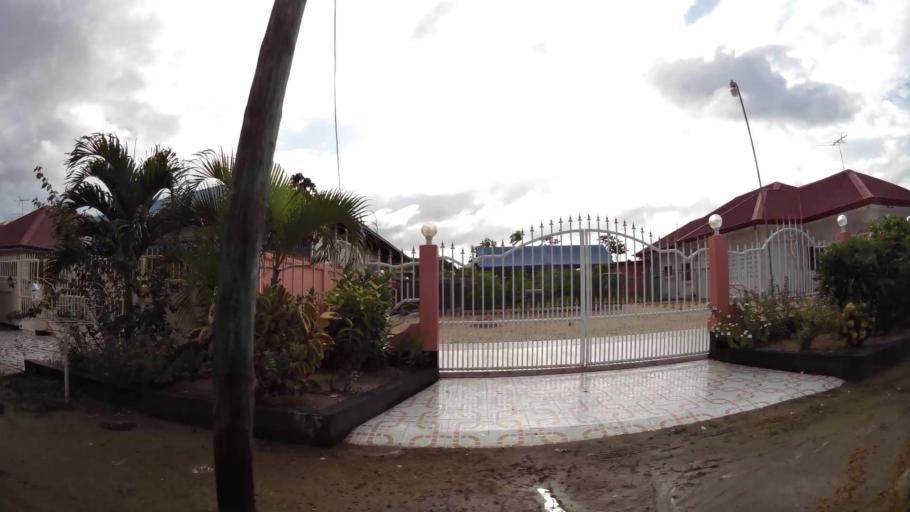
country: SR
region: Paramaribo
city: Paramaribo
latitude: 5.8525
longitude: -55.2321
